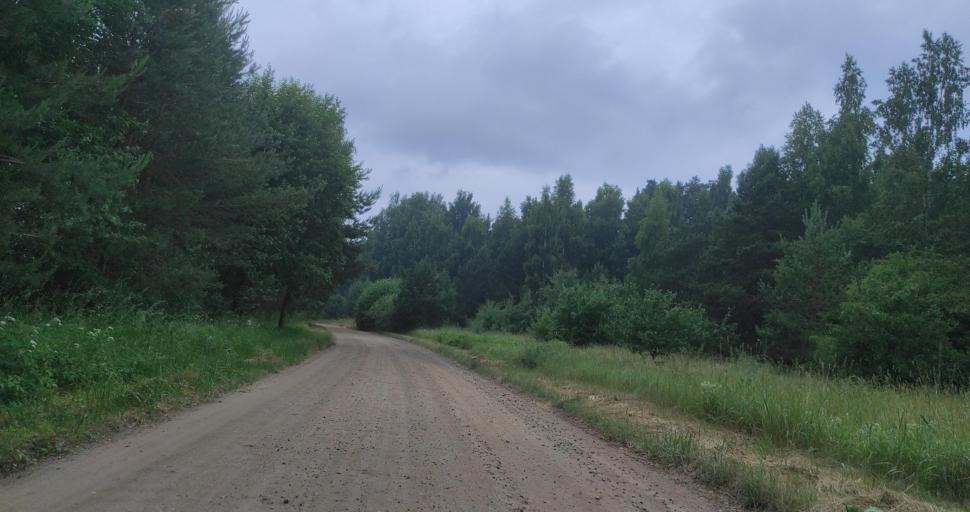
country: LV
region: Pavilostas
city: Pavilosta
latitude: 56.8850
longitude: 21.2076
